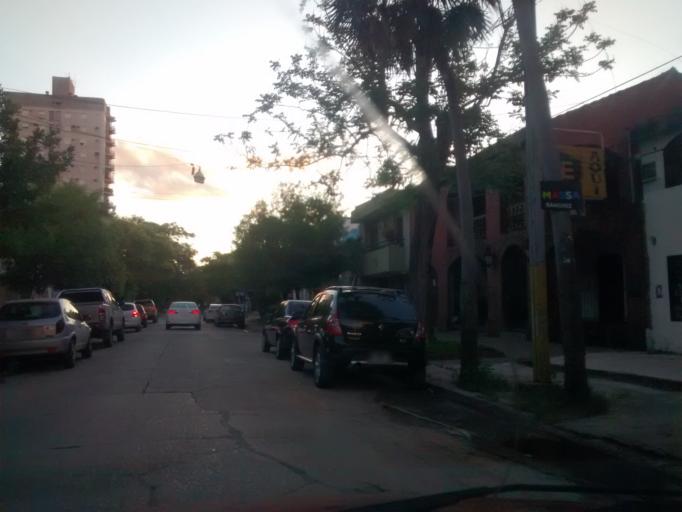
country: AR
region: Chaco
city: Resistencia
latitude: -27.4483
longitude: -58.9798
